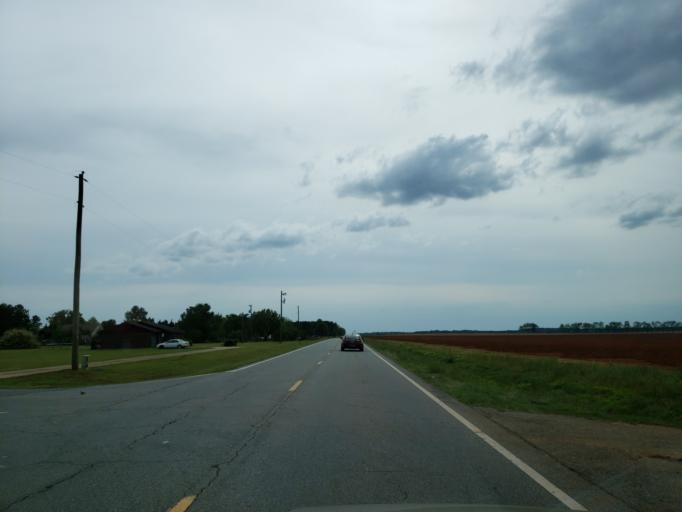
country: US
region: Georgia
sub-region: Houston County
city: Perry
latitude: 32.4334
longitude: -83.8076
